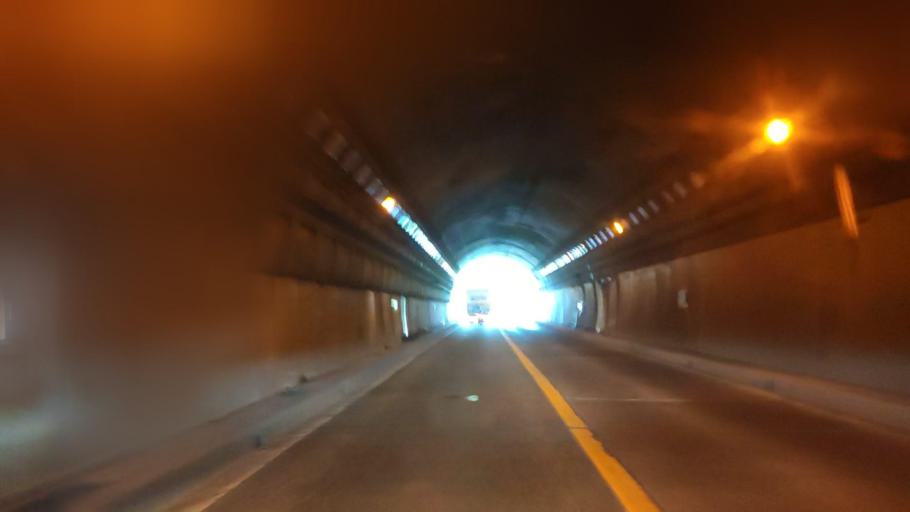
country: JP
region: Shizuoka
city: Fujinomiya
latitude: 35.2087
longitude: 138.5164
